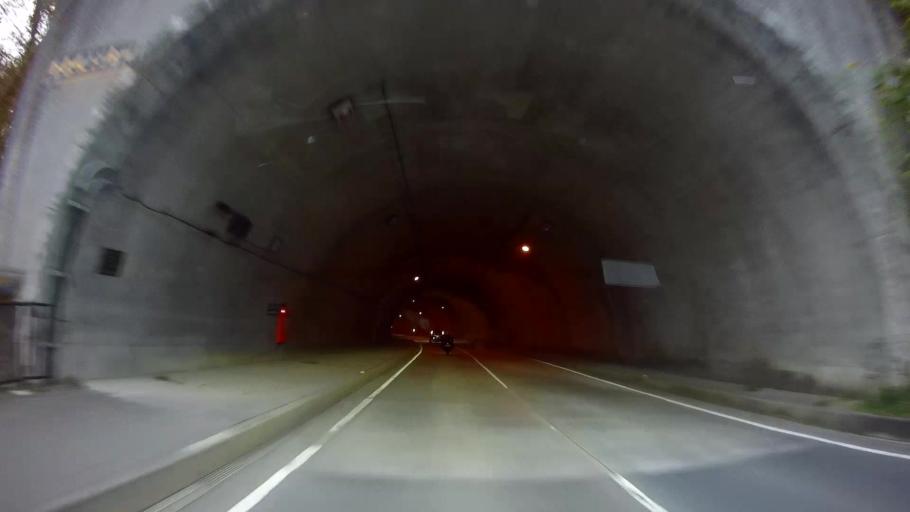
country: JP
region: Gunma
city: Nakanojomachi
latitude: 36.5519
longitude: 138.7136
